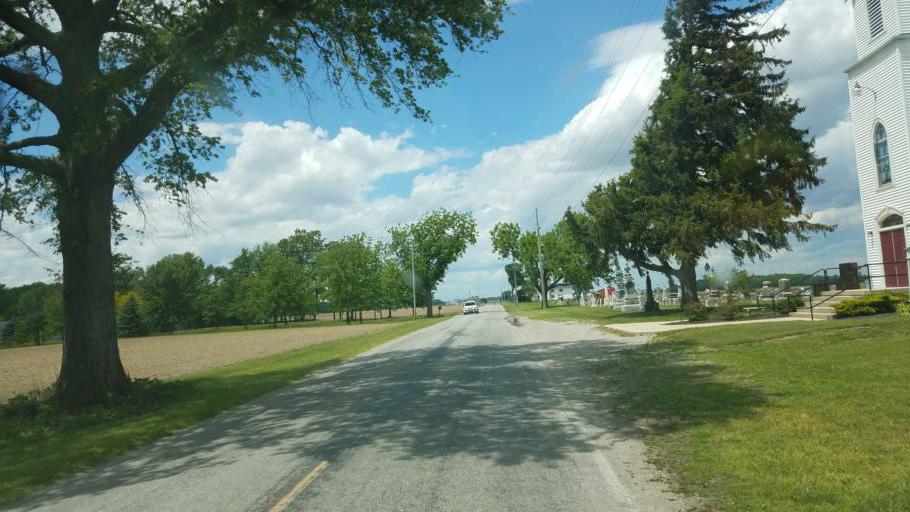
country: US
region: Ohio
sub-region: Huron County
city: Monroeville
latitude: 41.1917
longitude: -82.7285
